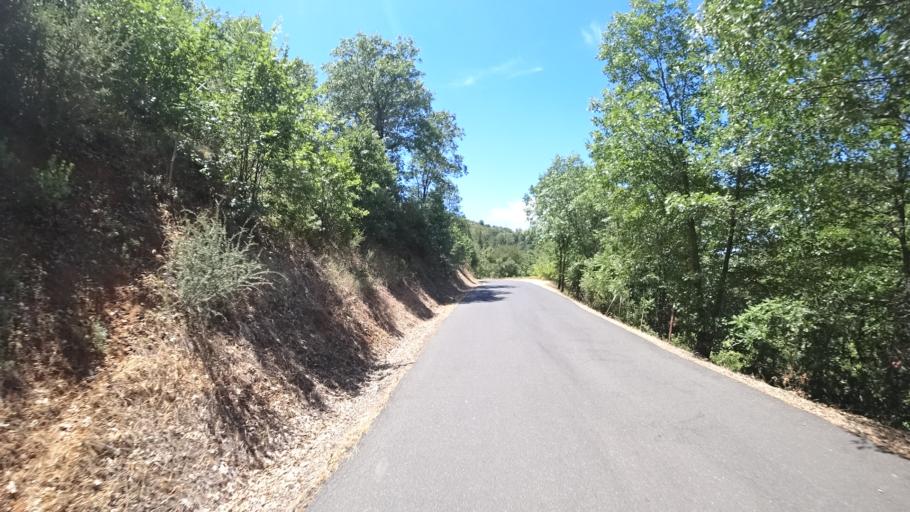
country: US
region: California
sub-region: Calaveras County
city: Forest Meadows
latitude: 38.1856
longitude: -120.4487
